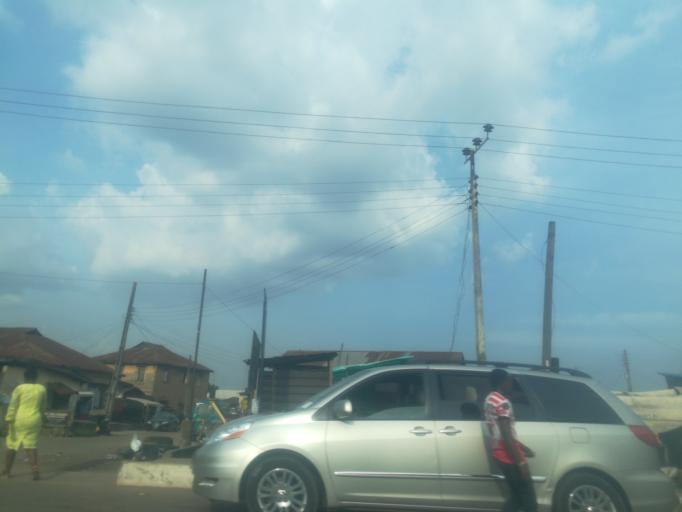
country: NG
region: Ogun
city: Abeokuta
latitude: 7.1395
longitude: 3.3313
